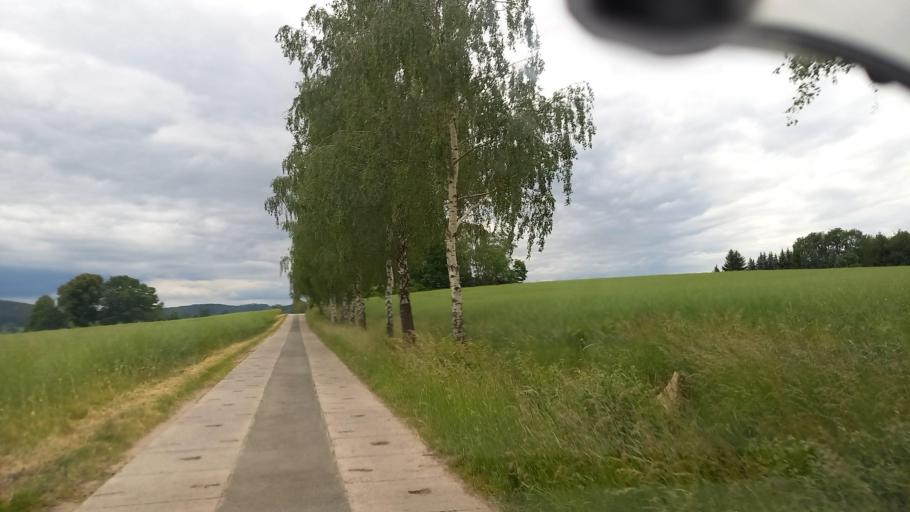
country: DE
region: Saxony
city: Kirchberg
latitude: 50.6002
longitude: 12.5406
